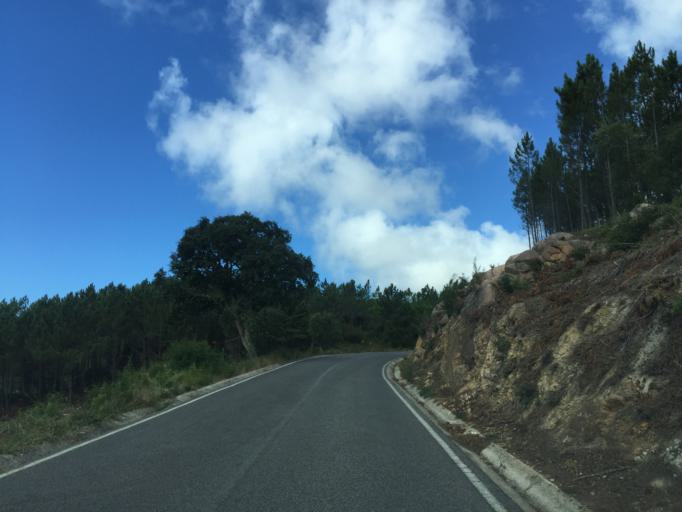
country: PT
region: Lisbon
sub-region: Cascais
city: Alcabideche
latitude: 38.7582
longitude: -9.4337
